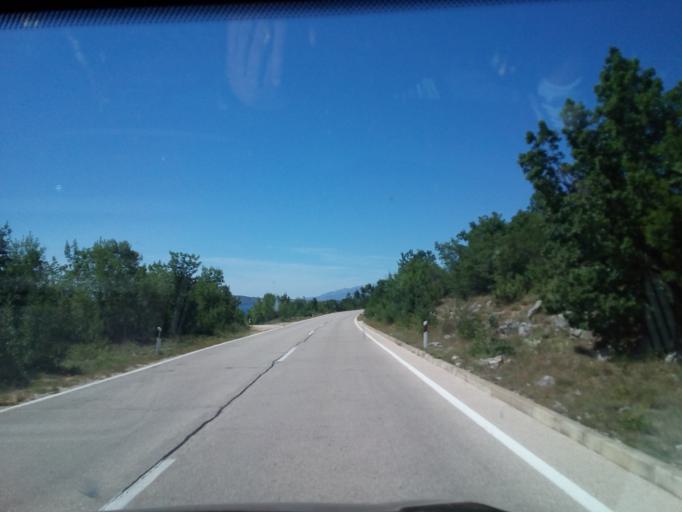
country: HR
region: Zadarska
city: Krusevo
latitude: 44.1733
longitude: 15.6199
